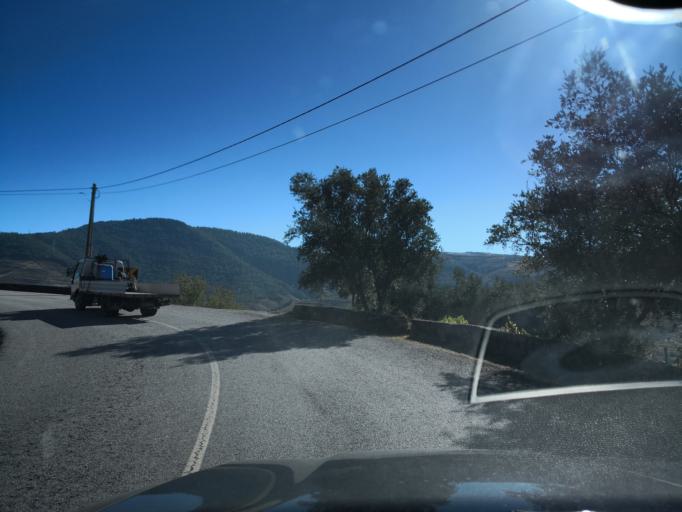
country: PT
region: Viseu
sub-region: Tabuaco
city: Tabuaco
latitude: 41.1671
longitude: -7.5351
